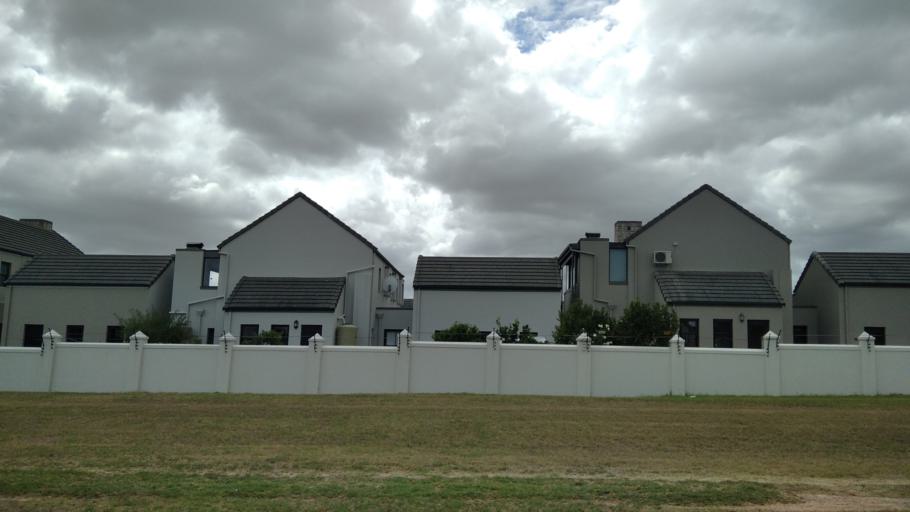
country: ZA
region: Western Cape
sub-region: City of Cape Town
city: Kraaifontein
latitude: -33.8193
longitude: 18.6774
